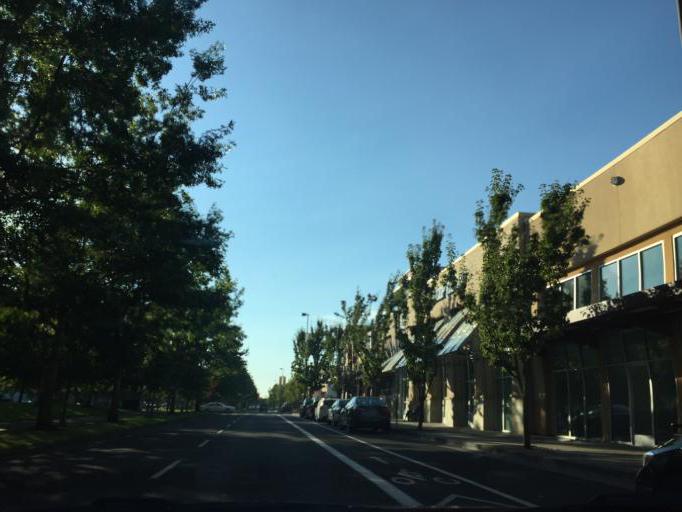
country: US
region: Washington
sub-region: Clark County
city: Orchards
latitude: 45.5731
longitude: -122.5587
